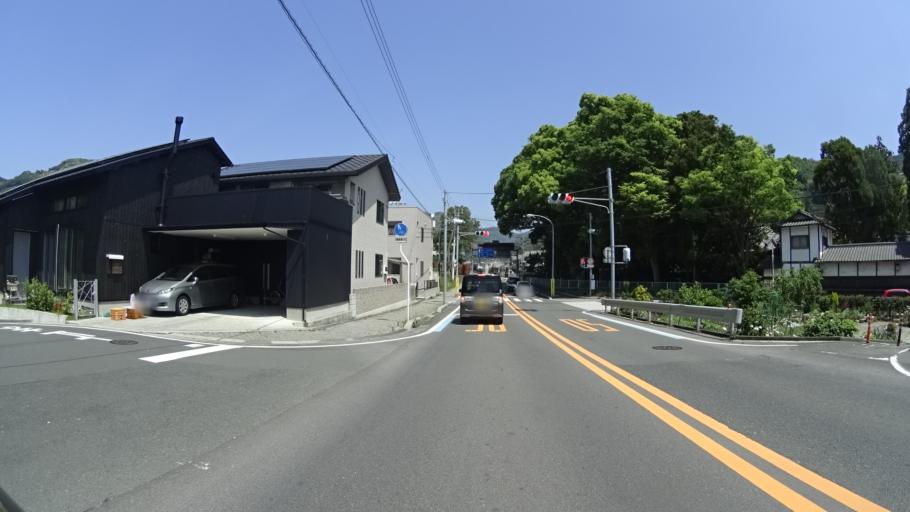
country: JP
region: Ehime
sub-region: Nishiuwa-gun
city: Ikata-cho
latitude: 33.4902
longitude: 132.3976
